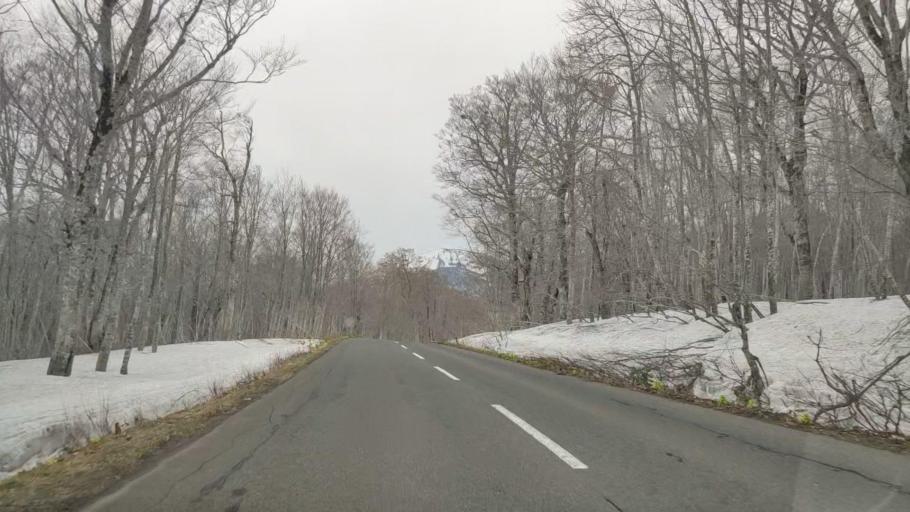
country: JP
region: Aomori
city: Aomori Shi
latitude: 40.6397
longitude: 140.9323
